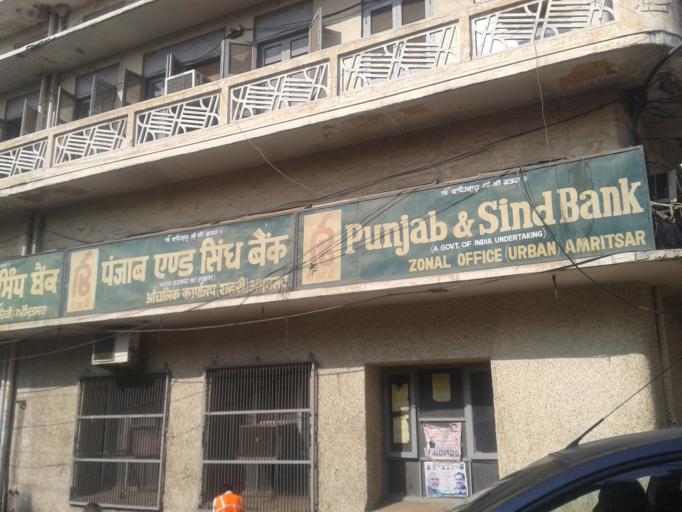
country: IN
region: Punjab
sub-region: Amritsar
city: Amritsar
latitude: 31.6263
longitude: 74.8783
